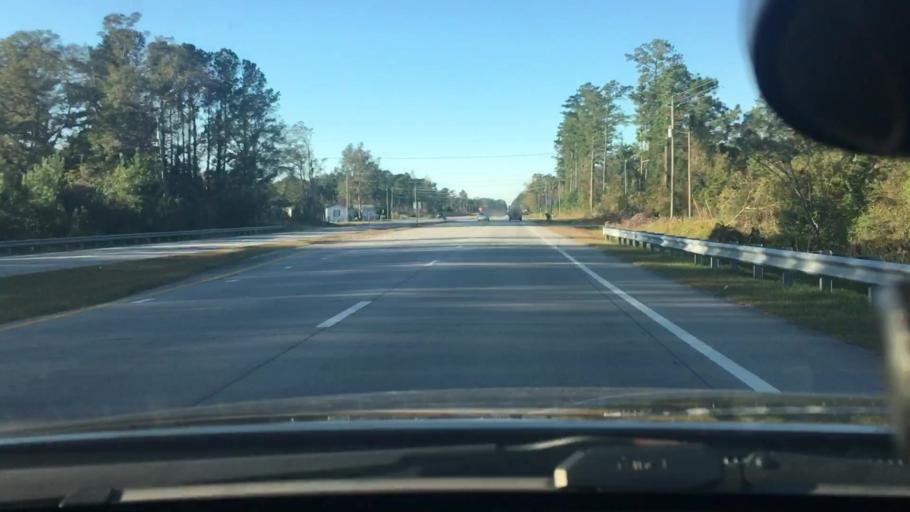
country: US
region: North Carolina
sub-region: Craven County
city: New Bern
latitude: 35.1448
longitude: -77.0312
